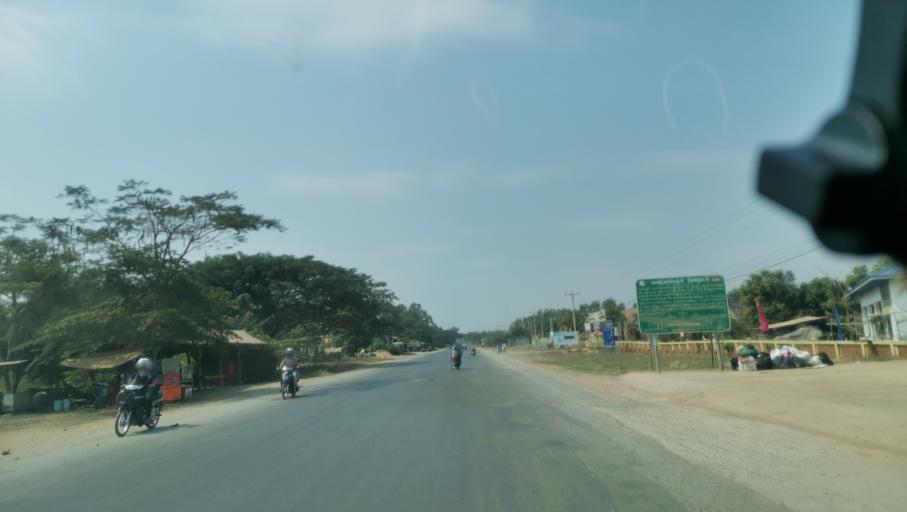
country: KH
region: Battambang
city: Battambang
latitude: 13.0719
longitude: 103.1687
